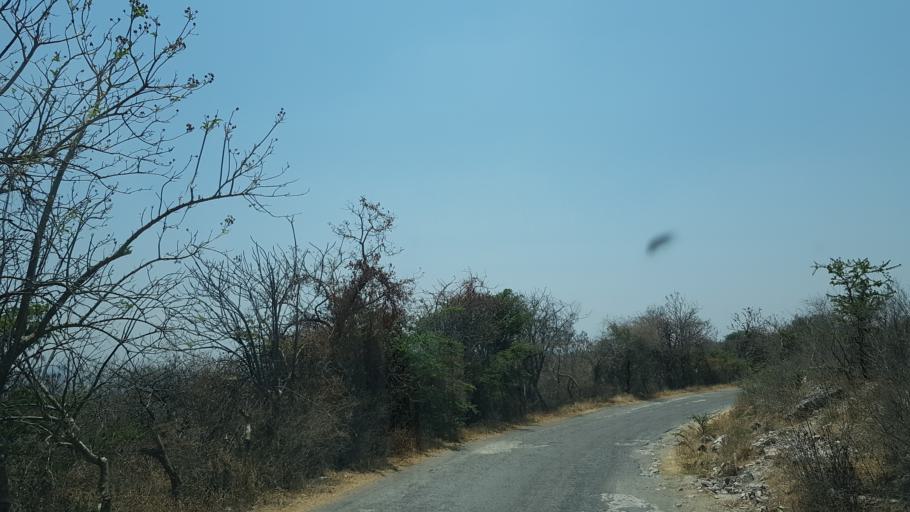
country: MX
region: Puebla
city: Huaquechula
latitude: 18.7887
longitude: -98.5439
